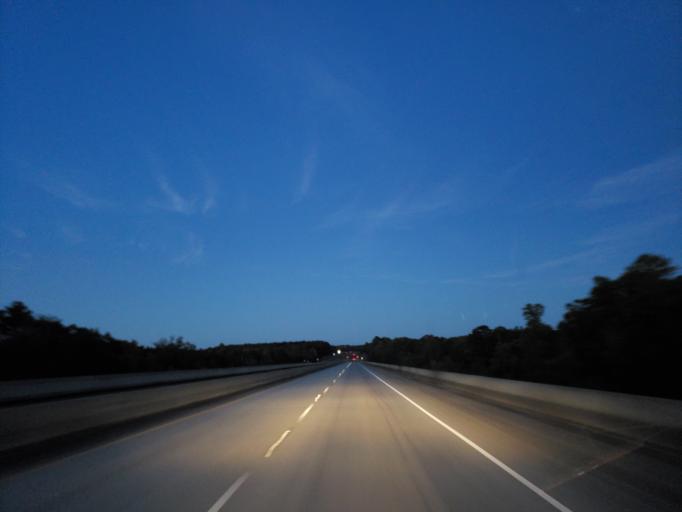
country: US
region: Mississippi
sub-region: Clarke County
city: Quitman
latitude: 31.9821
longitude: -88.7164
